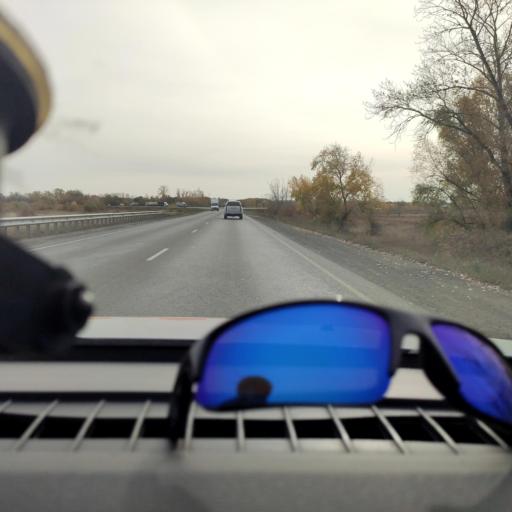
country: RU
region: Samara
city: Samara
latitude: 53.0947
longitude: 50.1477
